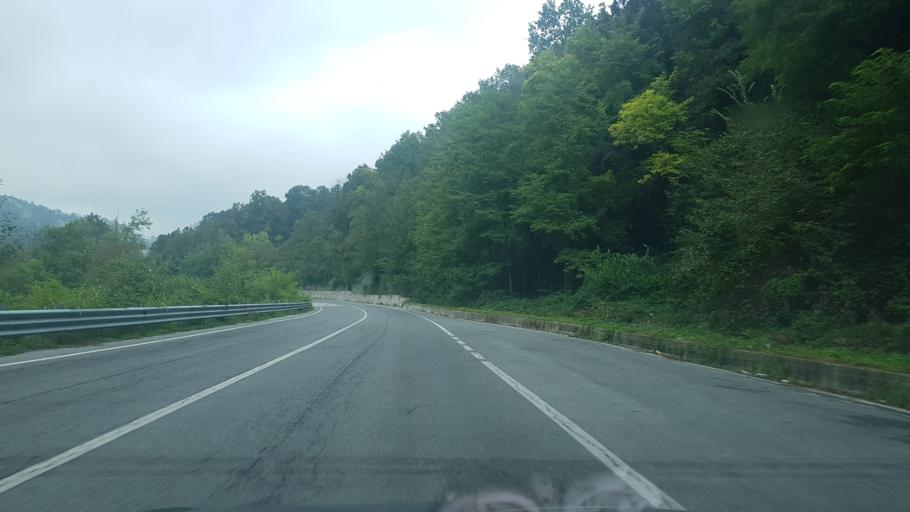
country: IT
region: Piedmont
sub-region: Provincia di Cuneo
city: Niella Tanaro
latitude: 44.4166
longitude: 7.9314
